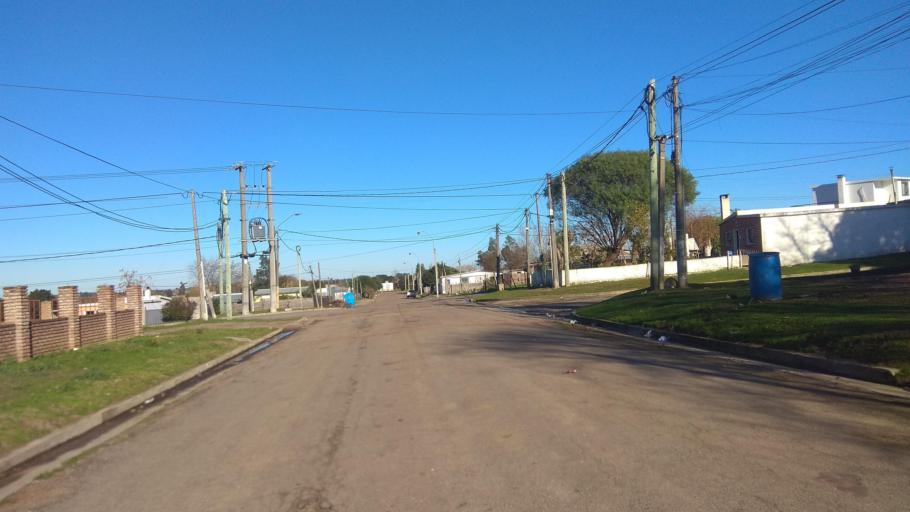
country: UY
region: Florida
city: Florida
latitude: -34.0979
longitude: -56.2382
